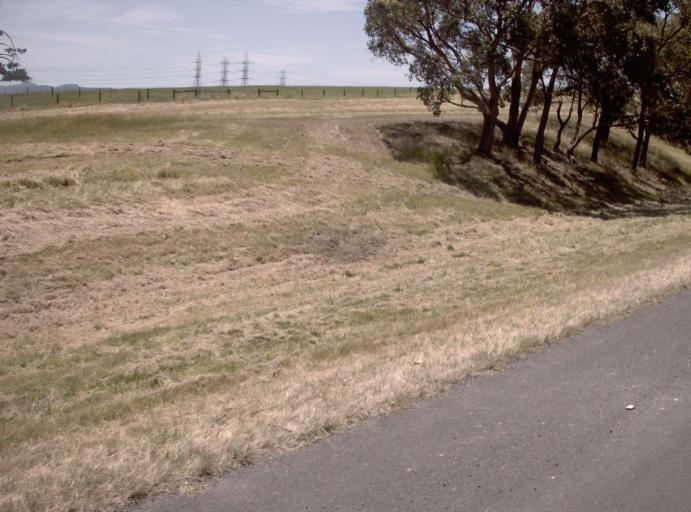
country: AU
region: Victoria
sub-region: Cardinia
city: Bunyip
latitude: -38.0773
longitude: 145.7370
